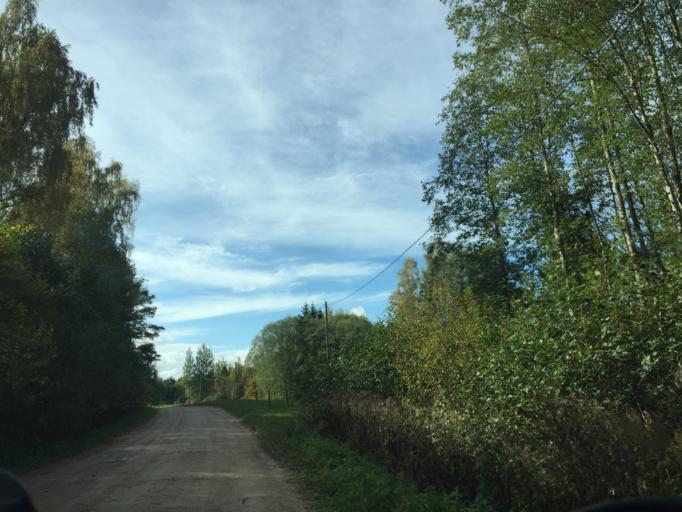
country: LV
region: Jaunpils
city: Jaunpils
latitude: 56.6099
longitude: 23.0036
